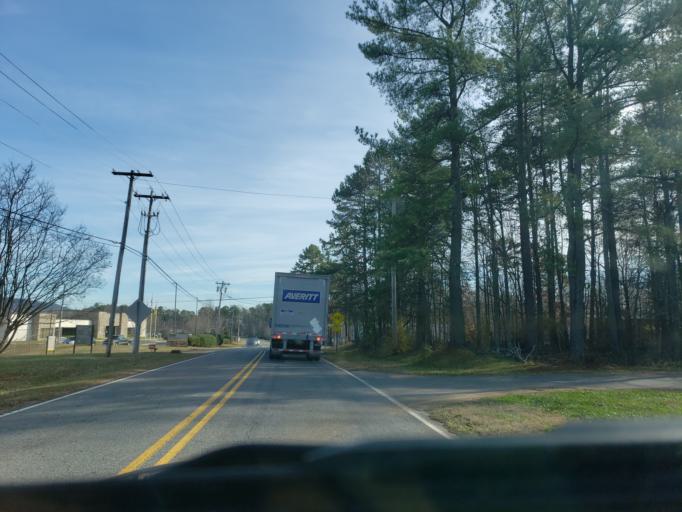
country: US
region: North Carolina
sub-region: Cleveland County
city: Kings Mountain
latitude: 35.2401
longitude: -81.3240
